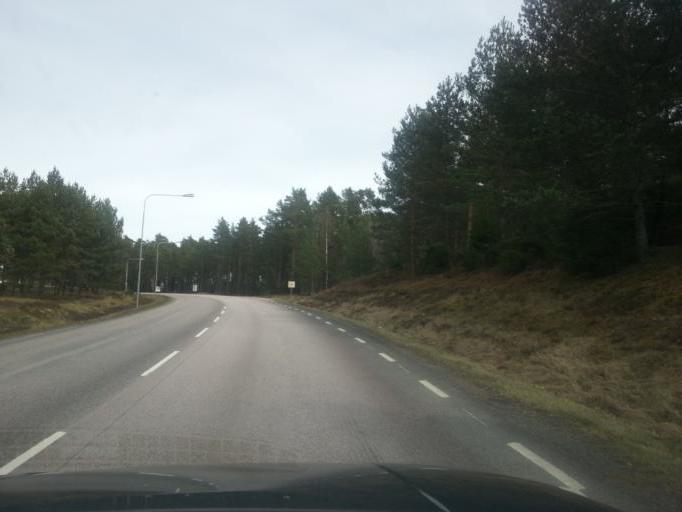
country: SE
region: Joenkoeping
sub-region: Jonkopings Kommun
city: Bankeryd
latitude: 57.8657
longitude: 14.1092
